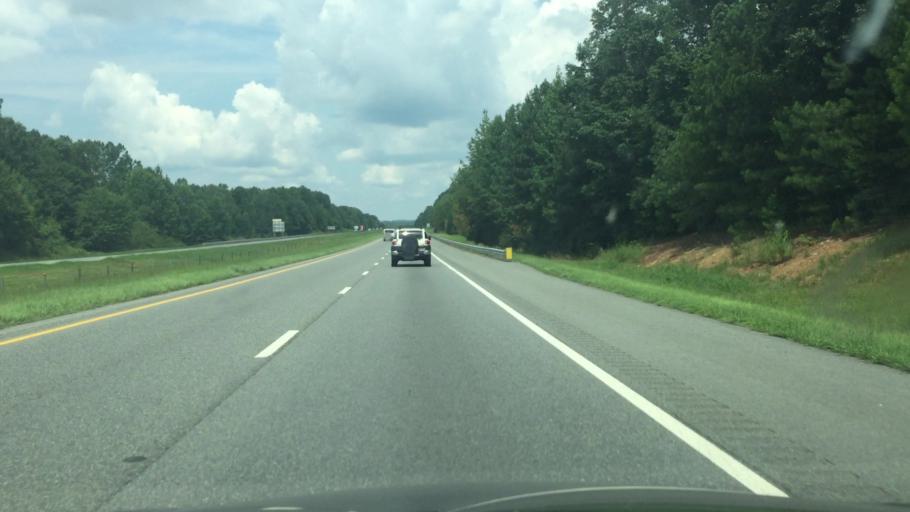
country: US
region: North Carolina
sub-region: Randolph County
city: Asheboro
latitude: 35.5436
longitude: -79.7944
